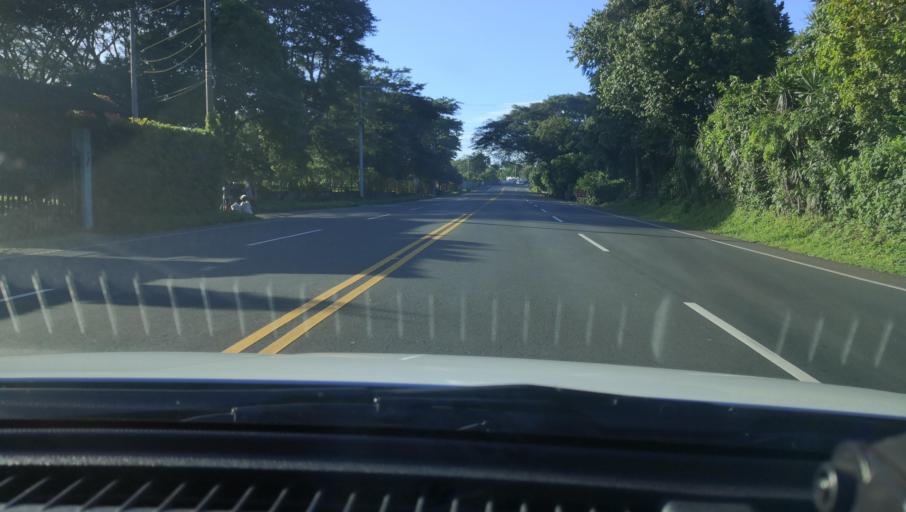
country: NI
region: Carazo
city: Diriamba
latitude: 11.8891
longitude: -86.2382
